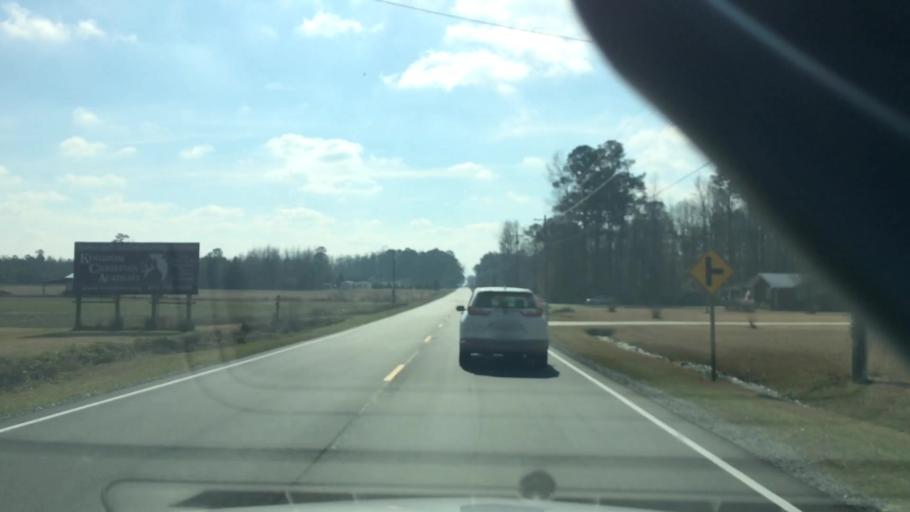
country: US
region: North Carolina
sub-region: Duplin County
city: Beulaville
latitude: 34.9694
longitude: -77.7626
